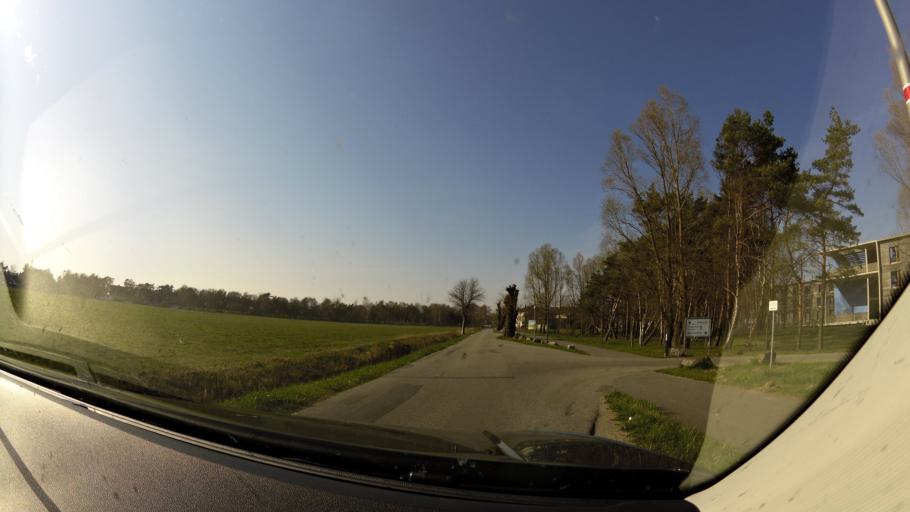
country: DE
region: Mecklenburg-Vorpommern
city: Ostseebad Dierhagen
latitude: 54.2986
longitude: 12.3483
